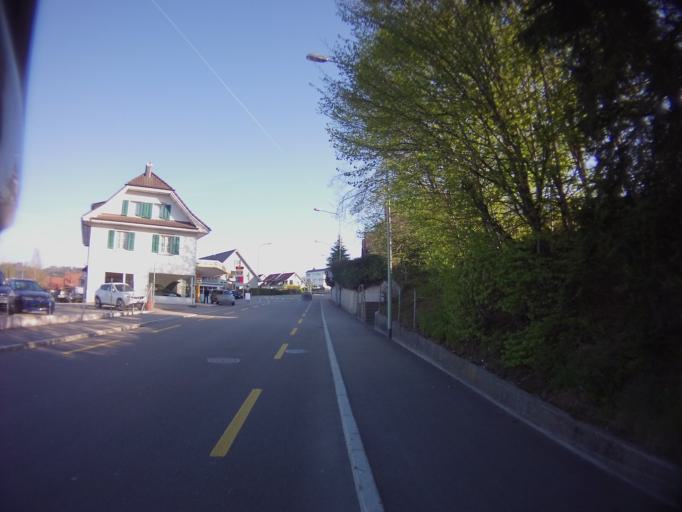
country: CH
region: Zurich
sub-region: Bezirk Affoltern
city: Hedingen
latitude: 47.3011
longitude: 8.4486
